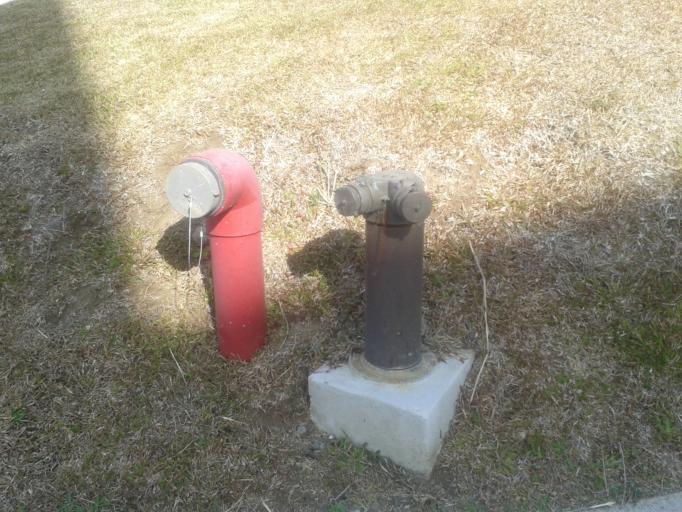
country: CR
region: San Jose
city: Sabanilla
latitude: 9.9381
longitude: -84.0416
